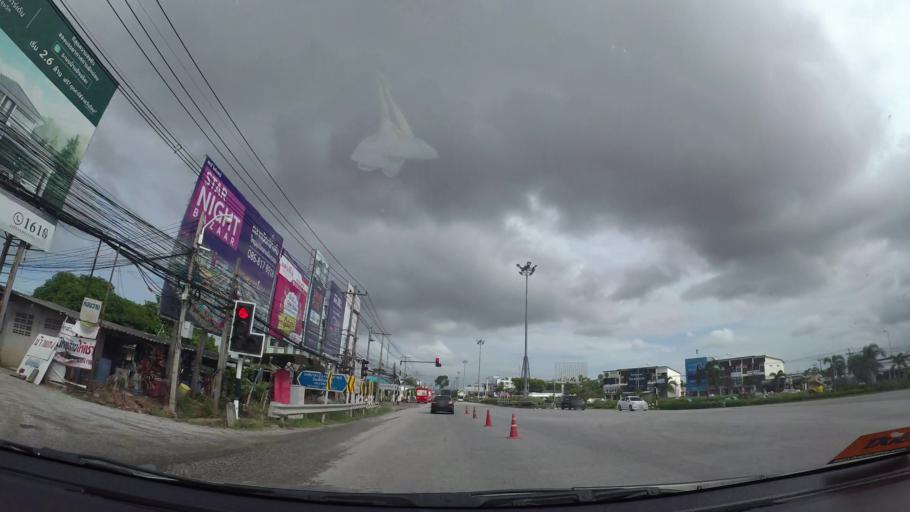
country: TH
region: Rayong
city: Rayong
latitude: 12.6901
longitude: 101.2070
